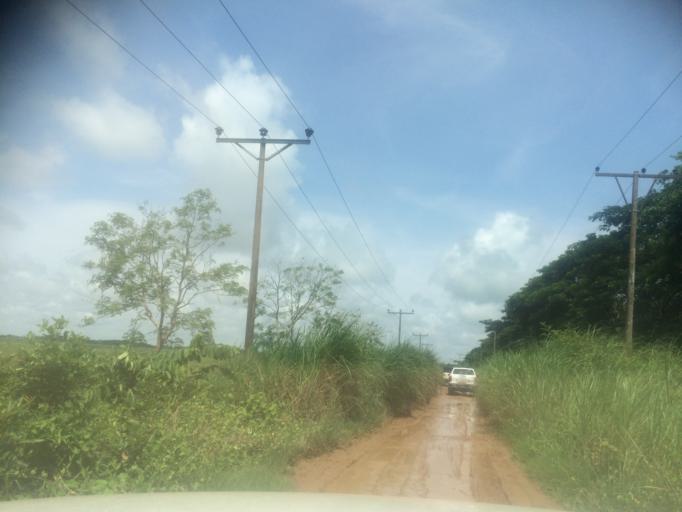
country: MM
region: Bago
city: Tharyarwady
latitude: 17.3174
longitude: 95.8944
